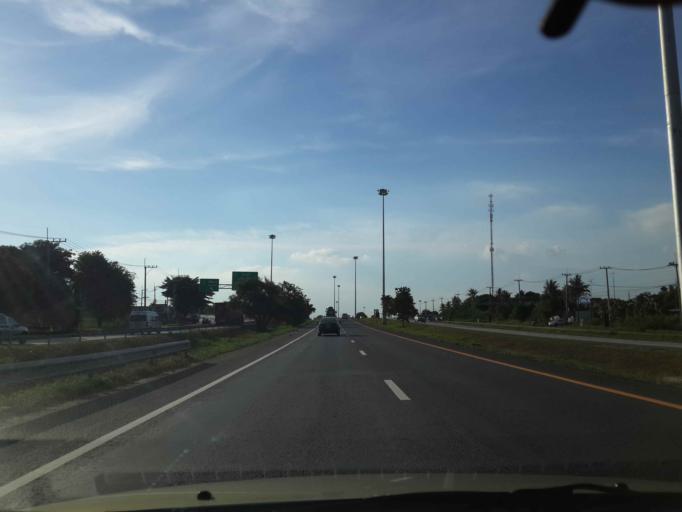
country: TH
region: Chon Buri
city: Bang Lamung
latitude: 12.9611
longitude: 100.9830
